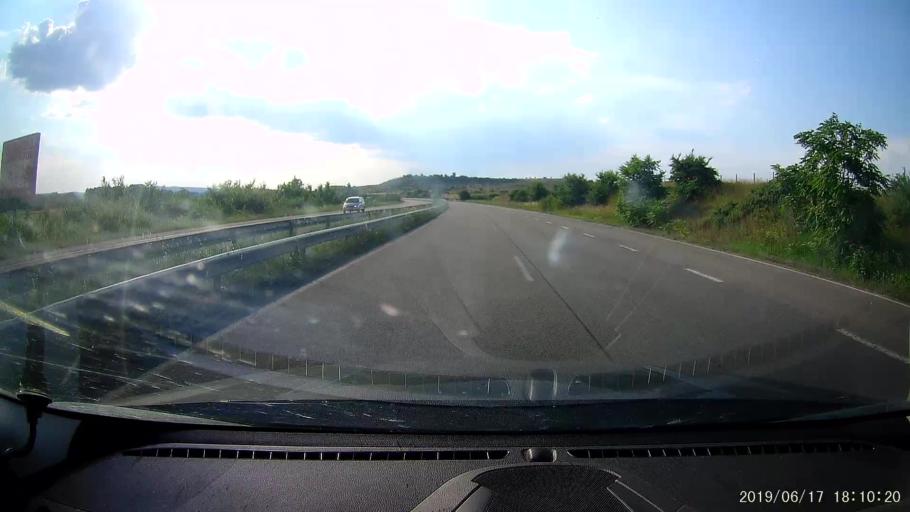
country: BG
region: Khaskovo
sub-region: Obshtina Lyubimets
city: Lyubimets
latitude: 41.8735
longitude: 26.0795
